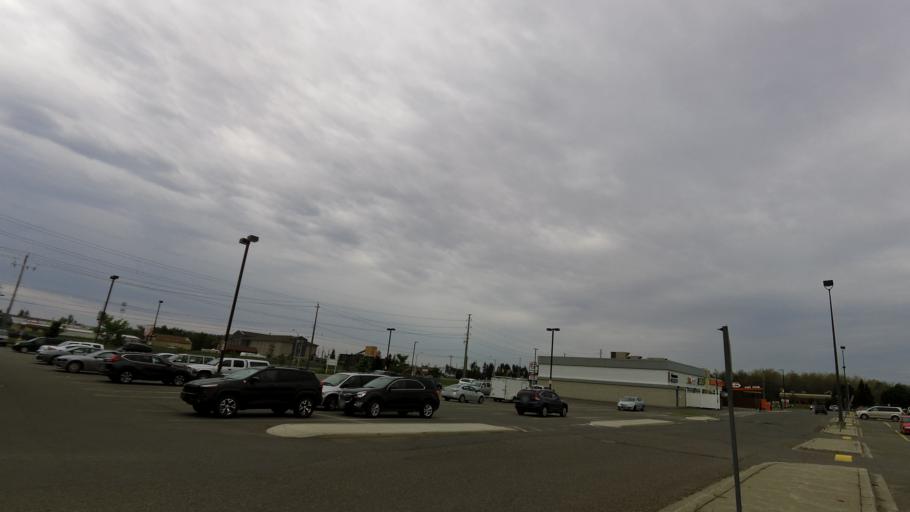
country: CA
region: Ontario
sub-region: Thunder Bay District
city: Thunder Bay
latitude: 48.4078
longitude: -89.2473
